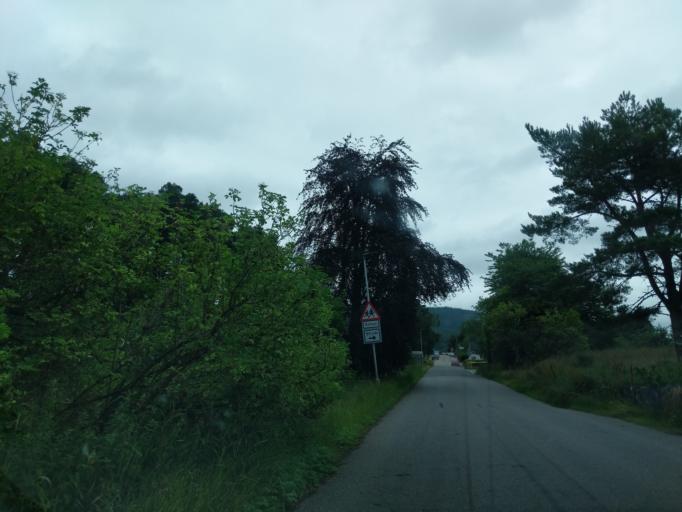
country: GB
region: Scotland
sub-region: Moray
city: Kinloss
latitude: 57.5511
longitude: -3.4712
